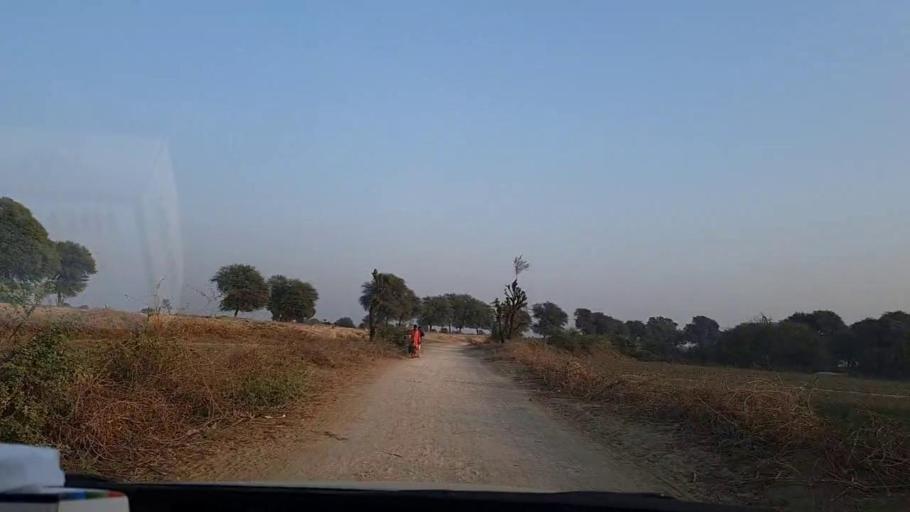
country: PK
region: Sindh
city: Tando Ghulam Ali
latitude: 25.1816
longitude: 68.9233
